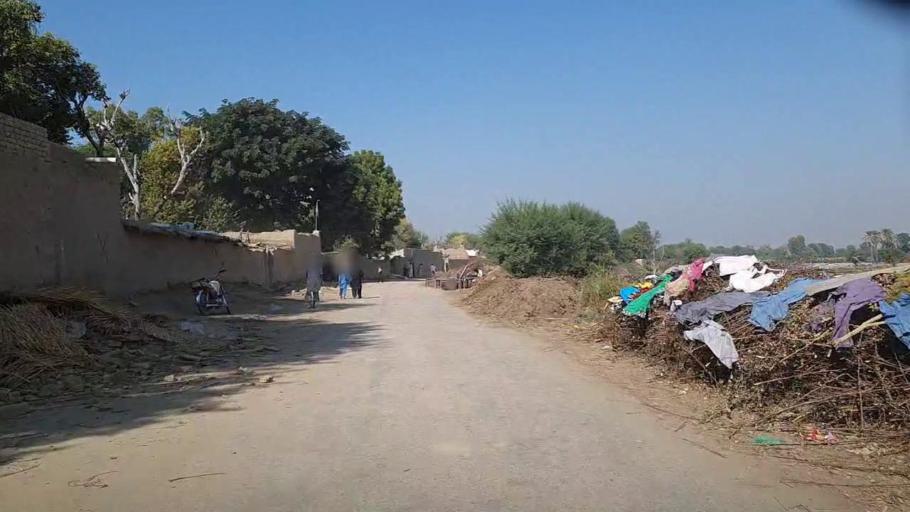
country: PK
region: Sindh
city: Bozdar
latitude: 27.1989
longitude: 68.6650
